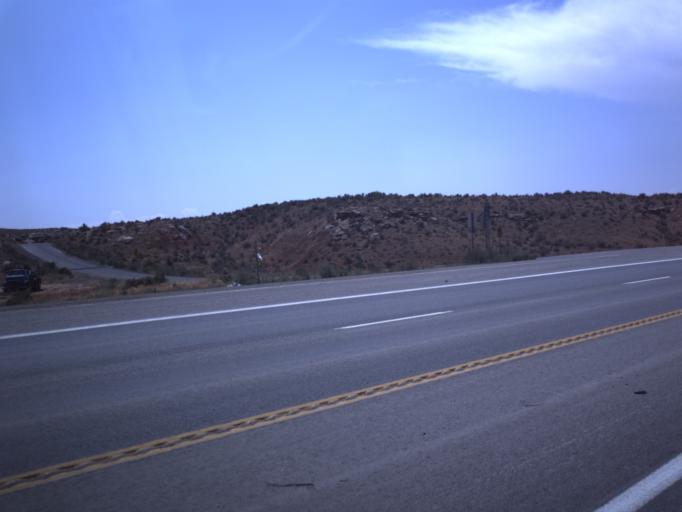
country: US
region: Utah
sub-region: Uintah County
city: Maeser
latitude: 40.3384
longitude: -109.6311
